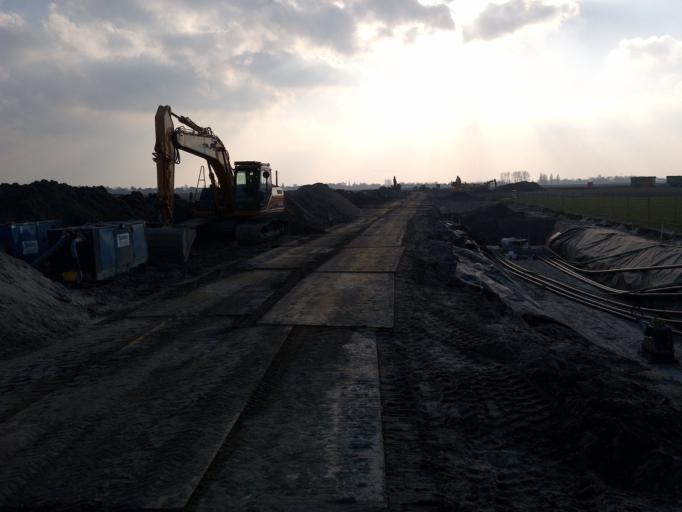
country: NL
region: South Holland
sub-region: Gemeente Rijnwoude
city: Benthuizen
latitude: 52.1087
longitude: 4.5750
